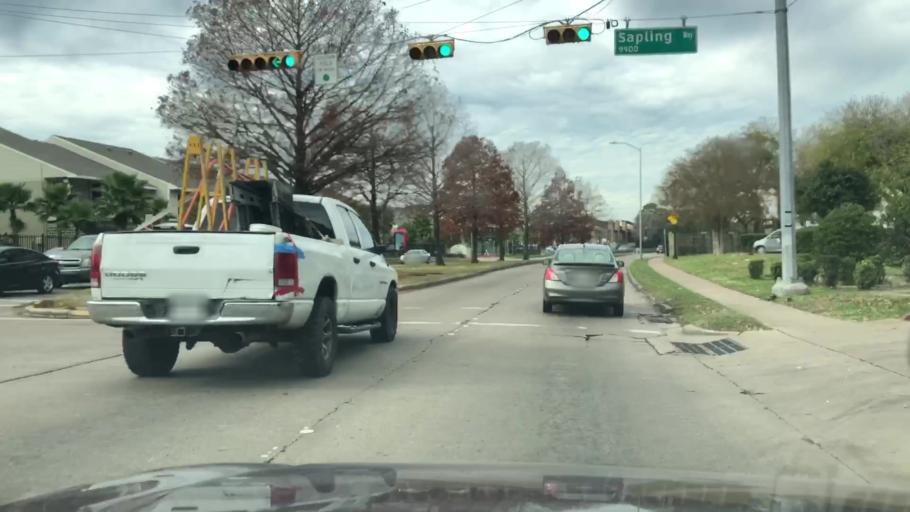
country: US
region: Texas
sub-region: Fort Bend County
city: Missouri City
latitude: 29.6718
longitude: -95.5316
